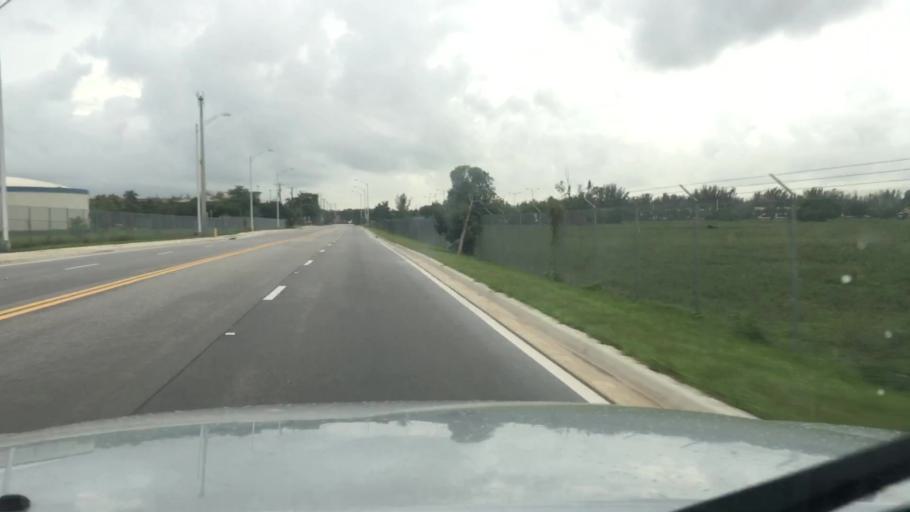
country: US
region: Florida
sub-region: Miami-Dade County
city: Doral
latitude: 25.8027
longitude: -80.3453
